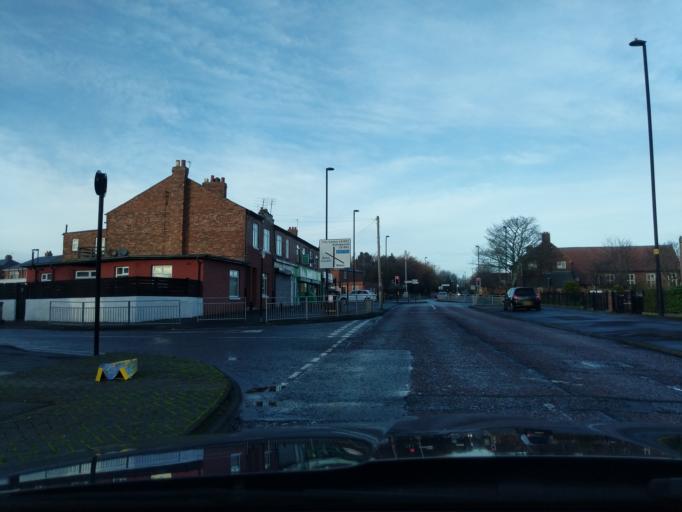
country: GB
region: England
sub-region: Gateshead
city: Felling
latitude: 54.9709
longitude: -1.5692
